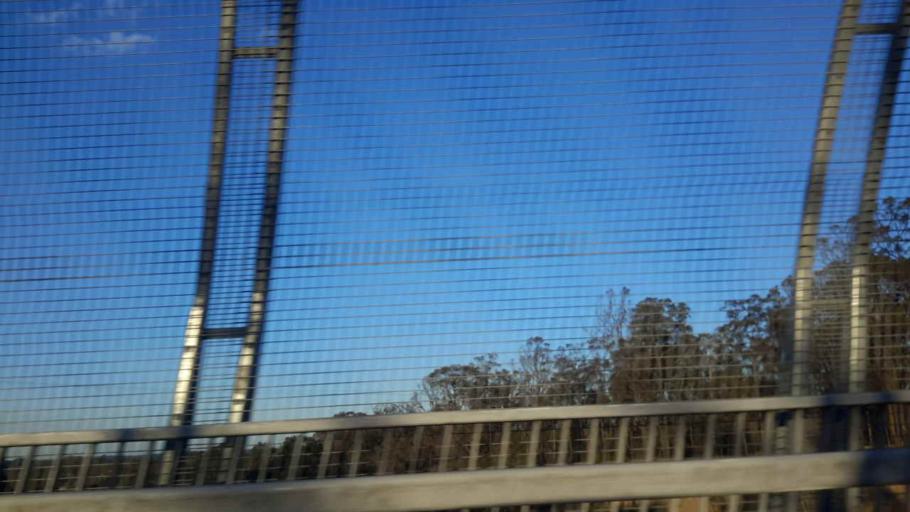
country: AU
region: New South Wales
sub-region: Wollondilly
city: Douglas Park
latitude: -34.1973
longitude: 150.7071
